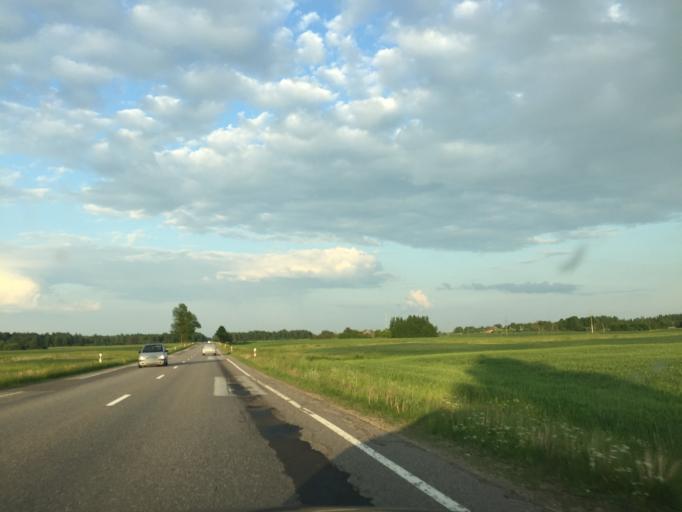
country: LT
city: Kursenai
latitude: 56.0049
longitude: 22.7280
